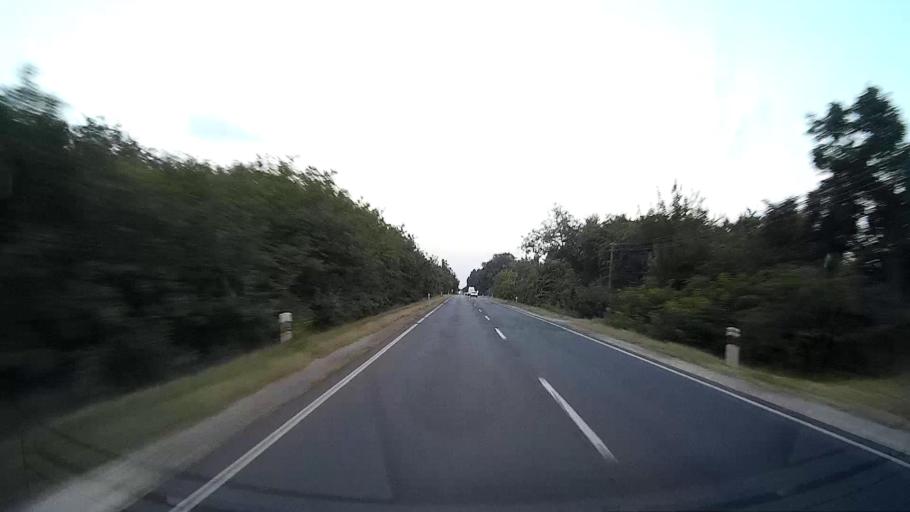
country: HU
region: Pest
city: Pilis
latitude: 47.2725
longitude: 19.5653
